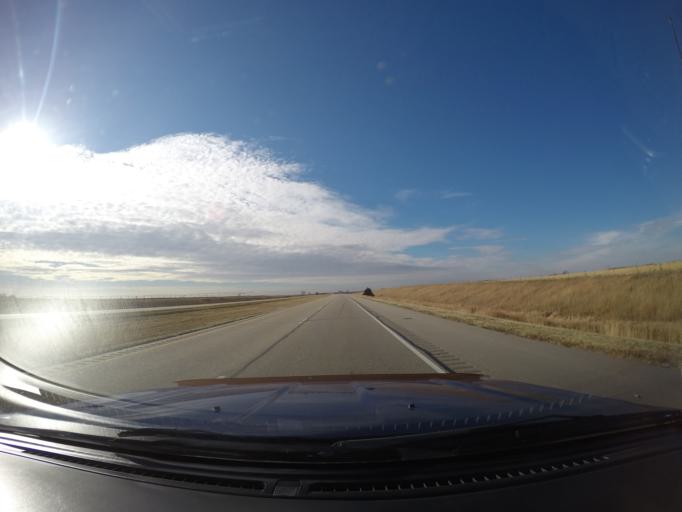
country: US
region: Nebraska
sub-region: Hall County
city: Grand Island
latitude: 40.8222
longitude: -98.1989
